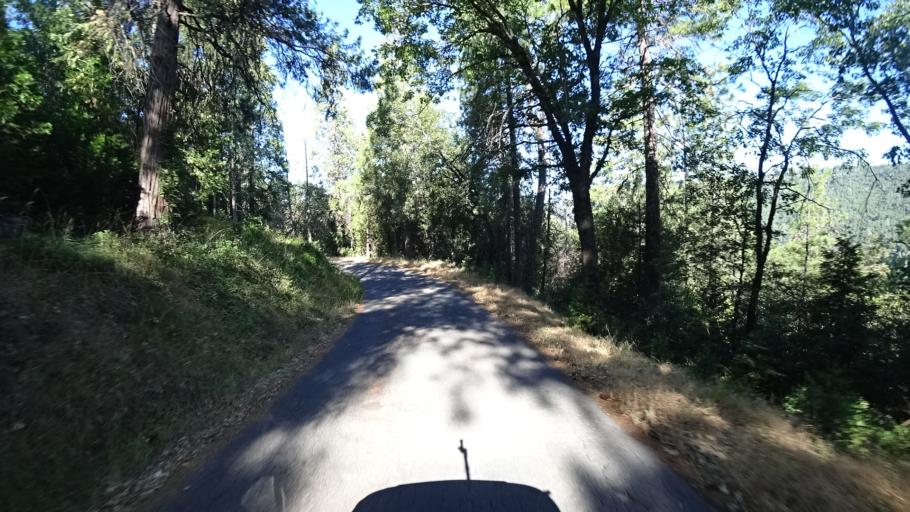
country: US
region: California
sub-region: Amador County
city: Pioneer
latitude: 38.3969
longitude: -120.5754
